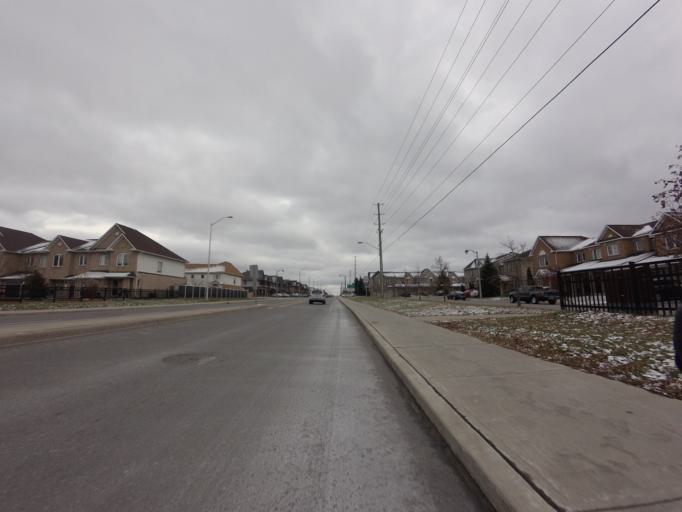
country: CA
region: Ontario
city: Bells Corners
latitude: 45.2734
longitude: -75.7173
